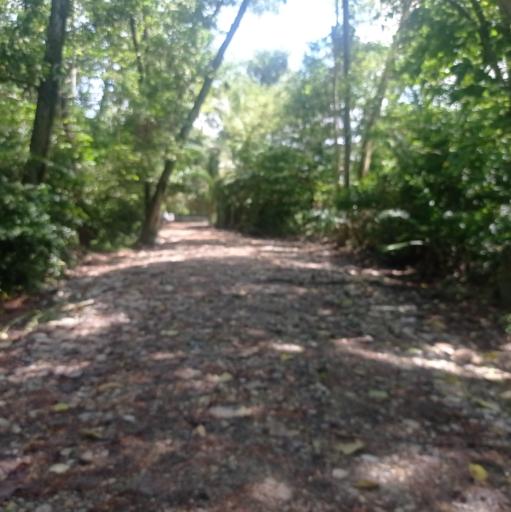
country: CO
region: Santander
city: Barrancabermeja
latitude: 7.1080
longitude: -73.8623
